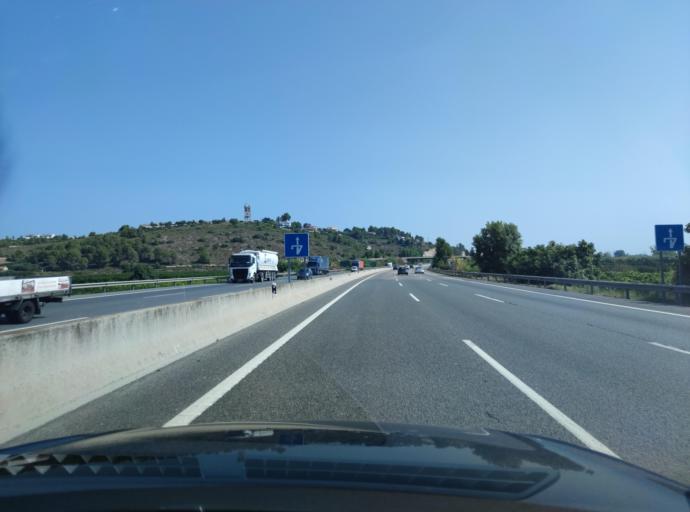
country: ES
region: Valencia
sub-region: Provincia de Valencia
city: Gavarda
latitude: 39.0825
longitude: -0.5409
